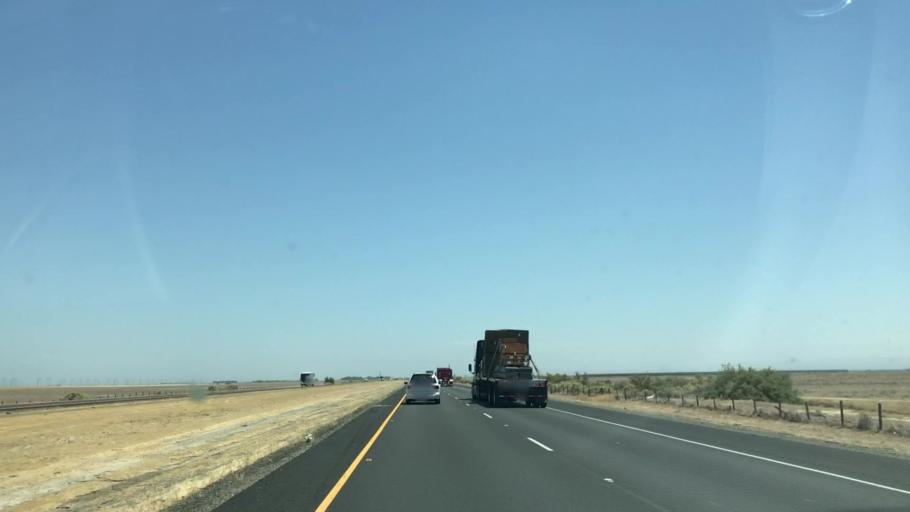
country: US
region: California
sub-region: Kern County
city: Lost Hills
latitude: 35.6598
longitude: -119.6858
